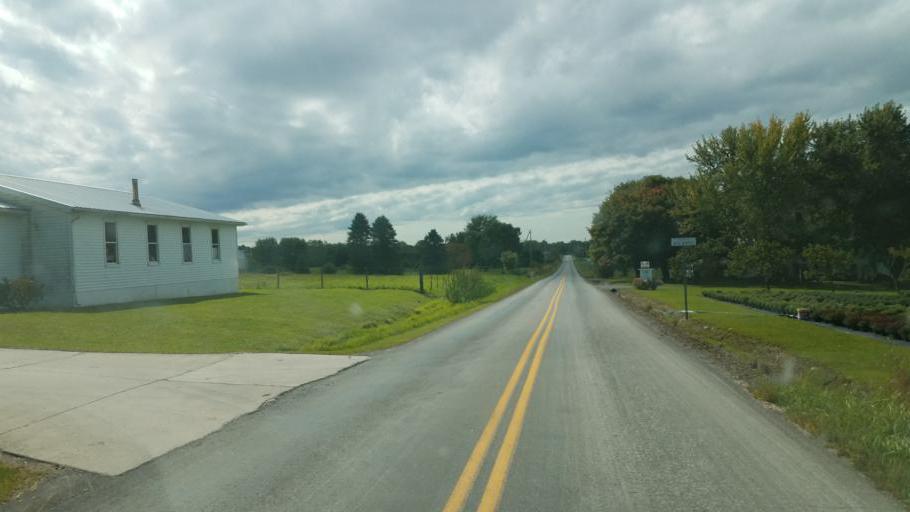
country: US
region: Pennsylvania
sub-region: Crawford County
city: Conneaut Lakeshore
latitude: 41.5117
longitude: -80.3376
